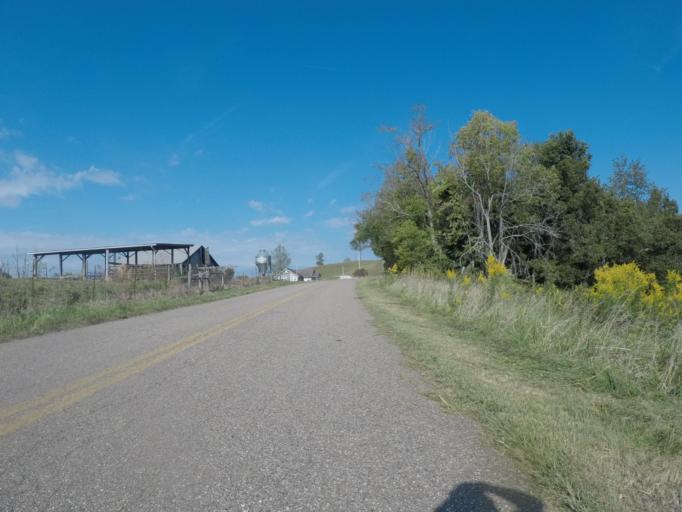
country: US
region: West Virginia
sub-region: Cabell County
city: Lesage
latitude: 38.6453
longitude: -82.4161
